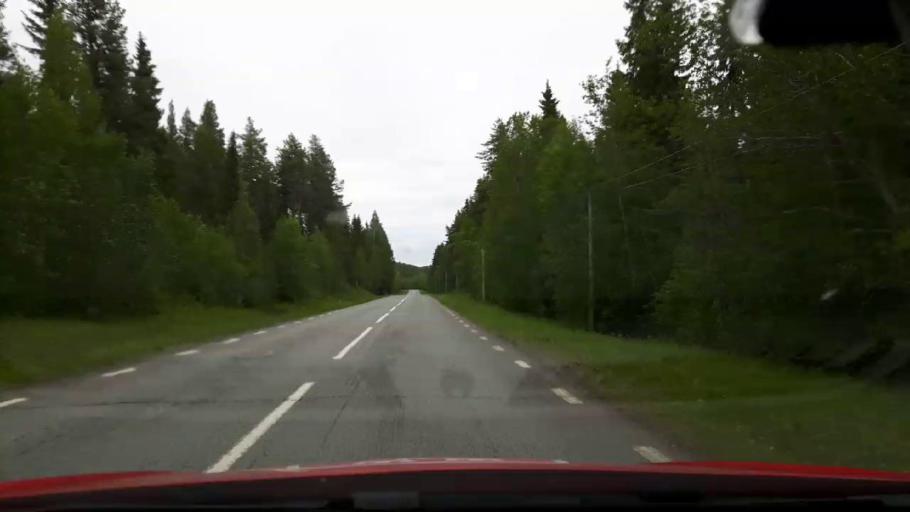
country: SE
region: Jaemtland
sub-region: Stroemsunds Kommun
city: Stroemsund
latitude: 63.3959
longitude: 15.6537
